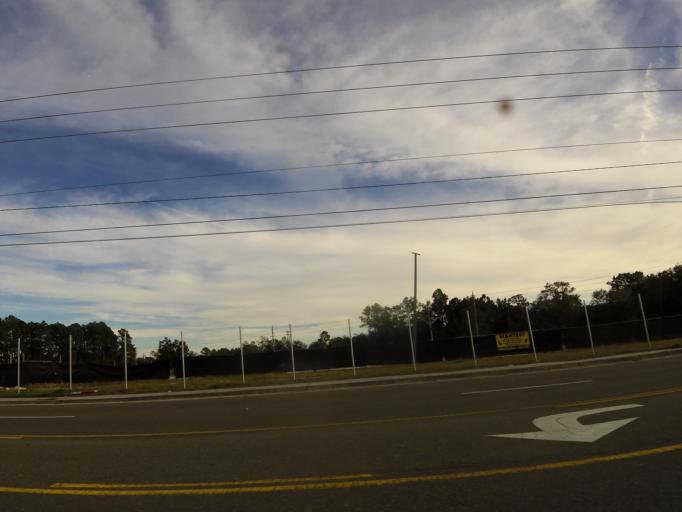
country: US
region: Florida
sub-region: Saint Johns County
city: Fruit Cove
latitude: 30.1627
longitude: -81.5420
